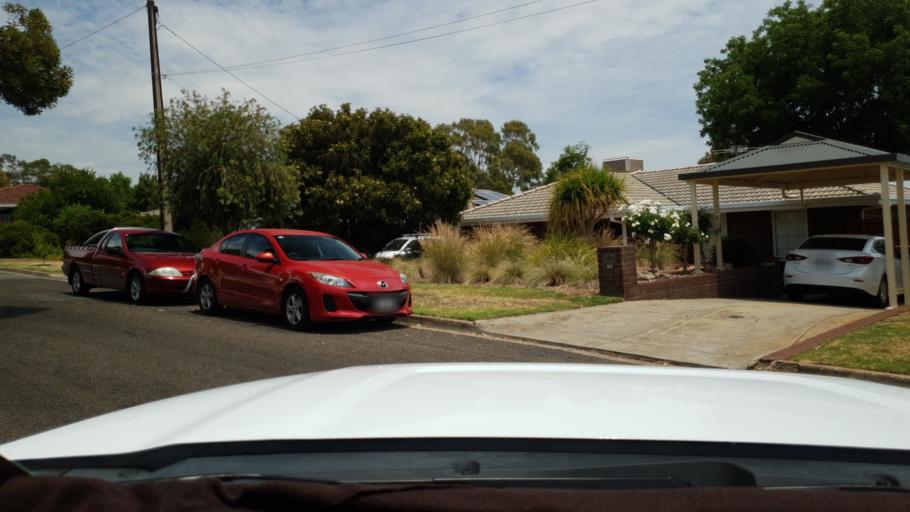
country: AU
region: South Australia
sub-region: Marion
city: Clovelly Park
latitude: -35.0026
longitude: 138.5853
